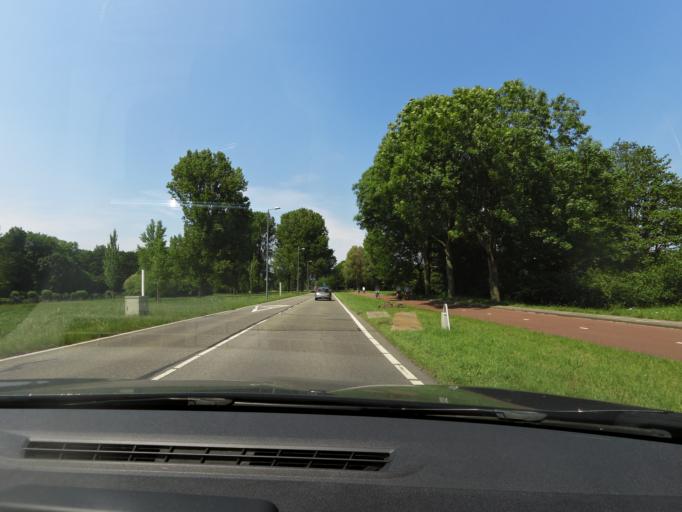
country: NL
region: South Holland
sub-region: Gemeente Rotterdam
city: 's-Gravenland
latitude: 51.9404
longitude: 4.5294
